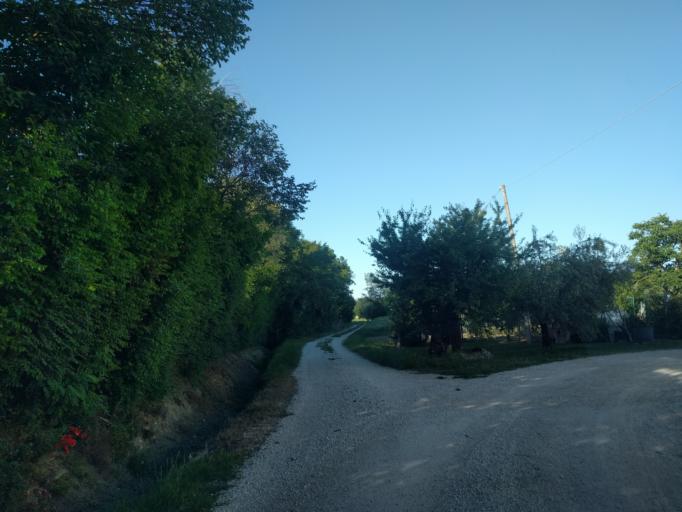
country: IT
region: The Marches
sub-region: Provincia di Pesaro e Urbino
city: Montemaggiore al Metauro
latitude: 43.7500
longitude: 12.9568
